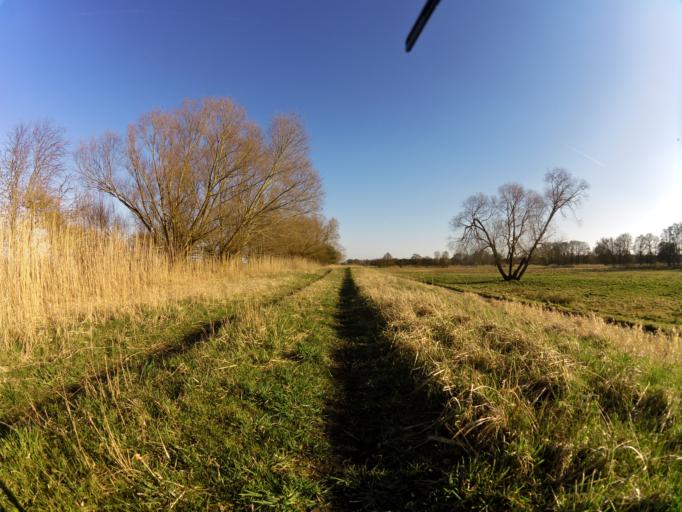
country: PL
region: West Pomeranian Voivodeship
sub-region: Powiat policki
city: Nowe Warpno
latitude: 53.7174
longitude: 14.3416
